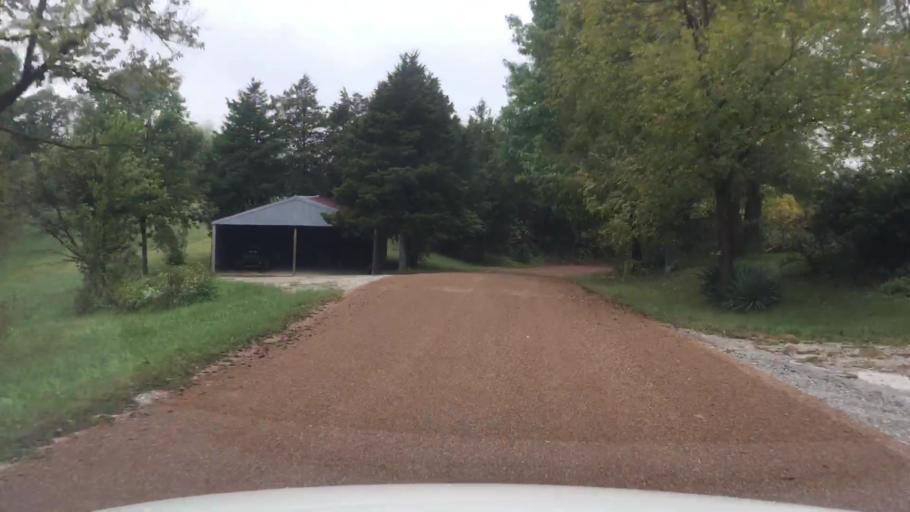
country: US
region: Missouri
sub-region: Boone County
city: Ashland
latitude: 38.8206
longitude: -92.3254
